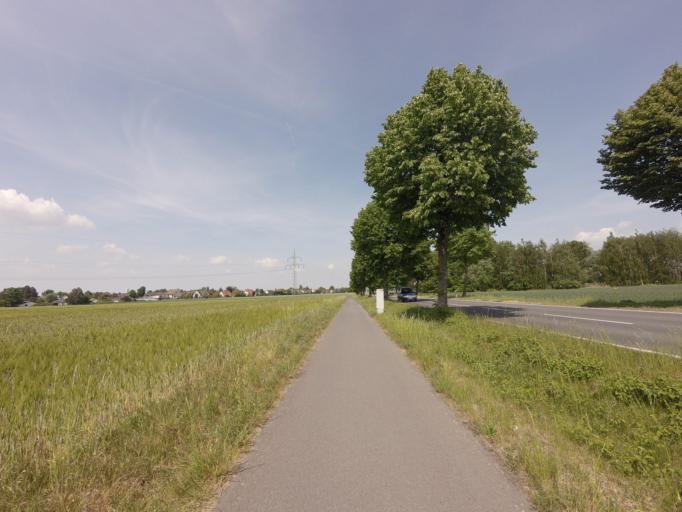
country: DE
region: Lower Saxony
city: Cremlingen
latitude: 52.2764
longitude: 10.6167
